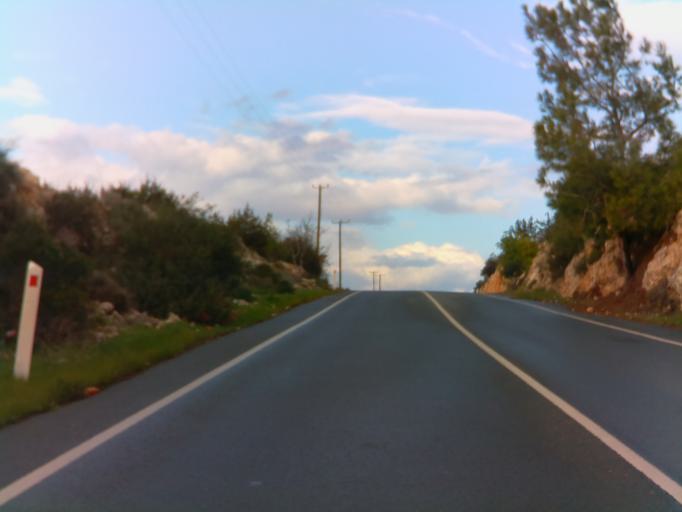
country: CY
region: Pafos
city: Pegeia
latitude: 34.8902
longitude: 32.3682
